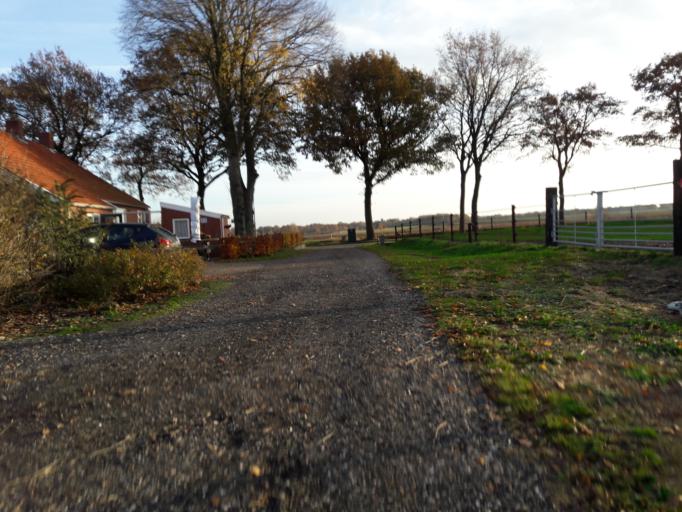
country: NL
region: Drenthe
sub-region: Gemeente Borger-Odoorn
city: Borger
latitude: 52.9567
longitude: 6.8156
